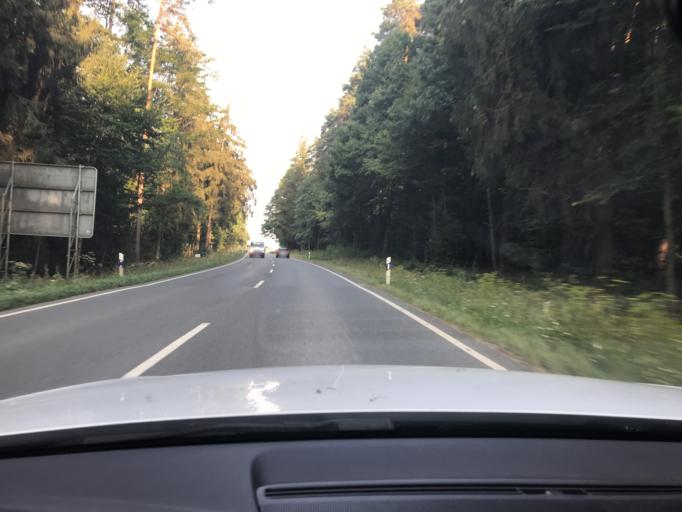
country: DE
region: Bavaria
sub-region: Regierungsbezirk Mittelfranken
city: Schnaittach
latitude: 49.5671
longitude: 11.3228
